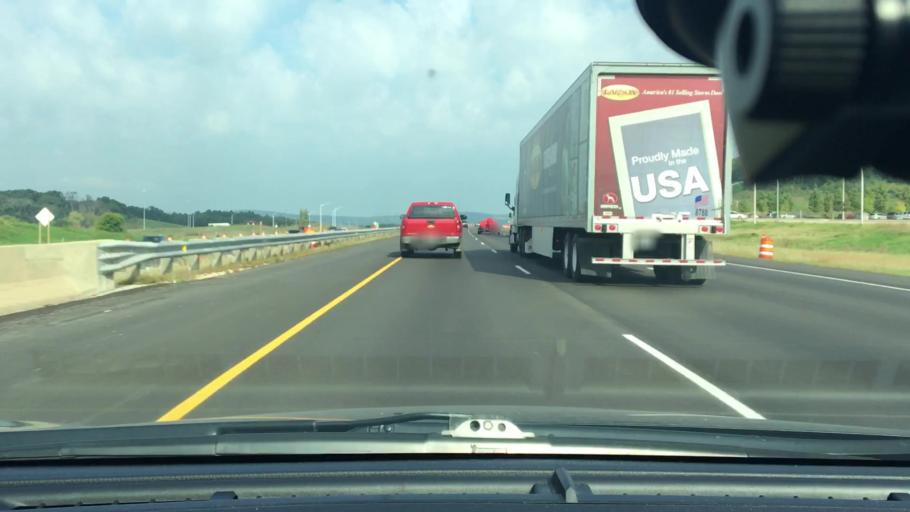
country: US
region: Wisconsin
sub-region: Columbia County
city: Poynette
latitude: 43.4234
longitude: -89.4763
